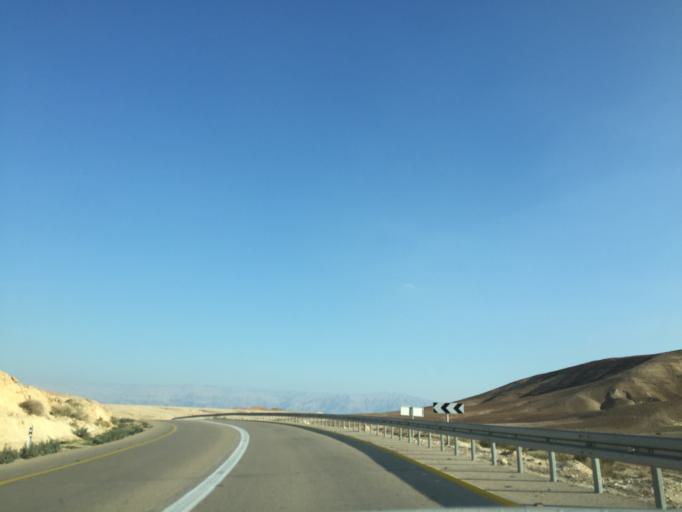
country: IL
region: Southern District
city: `En Boqeq
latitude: 31.1737
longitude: 35.3069
